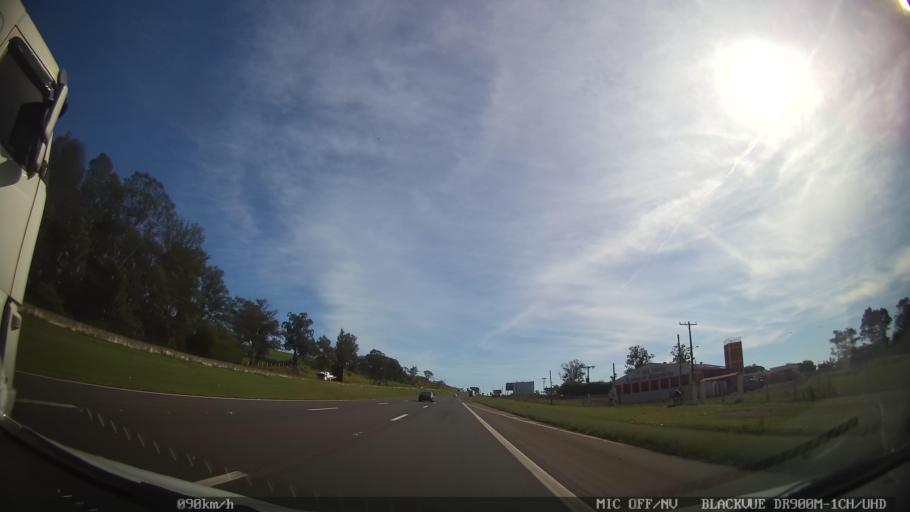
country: BR
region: Sao Paulo
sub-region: Araras
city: Araras
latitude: -22.3916
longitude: -47.3927
